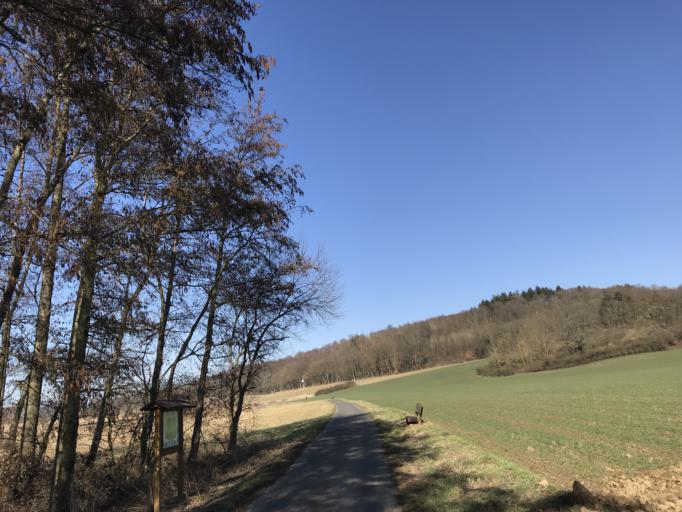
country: DE
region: Hesse
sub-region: Regierungsbezirk Darmstadt
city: Ranstadt
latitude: 50.3770
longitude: 8.9838
